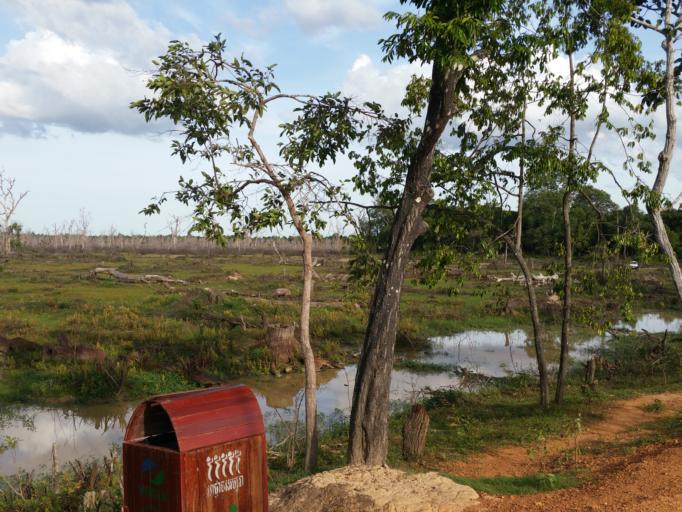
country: KH
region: Siem Reap
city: Siem Reap
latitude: 13.4666
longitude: 103.8948
